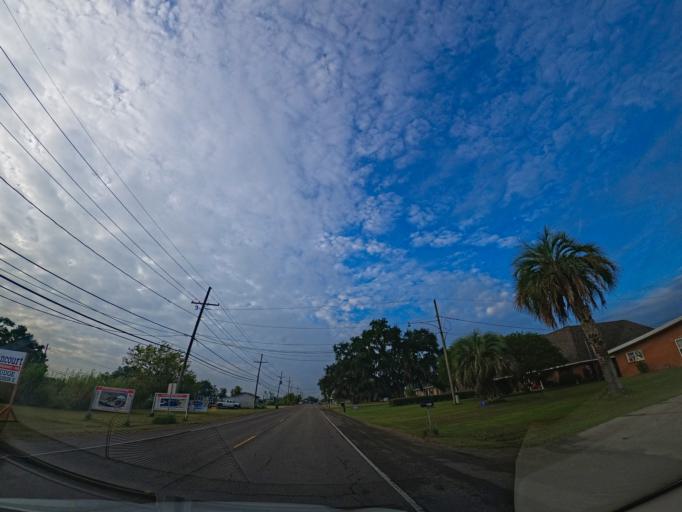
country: US
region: Louisiana
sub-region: Terrebonne Parish
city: Chauvin
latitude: 29.4418
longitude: -90.5945
